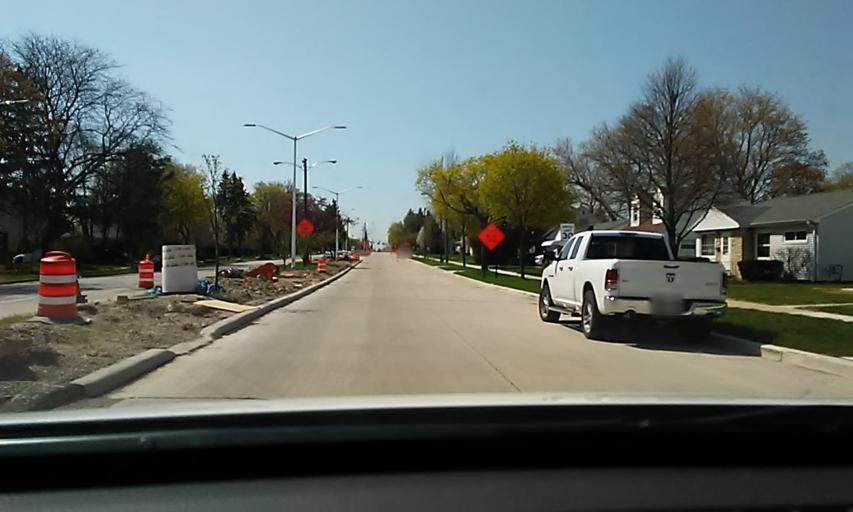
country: US
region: Wisconsin
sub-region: Milwaukee County
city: Greenfield
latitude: 42.9810
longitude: -87.9879
